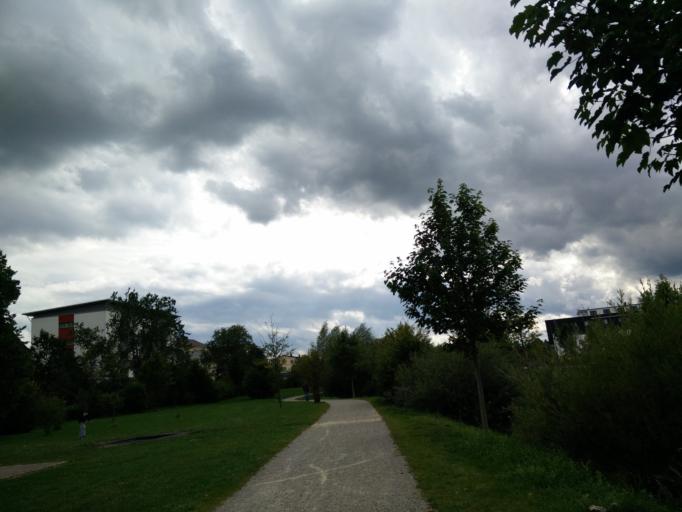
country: DE
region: Baden-Wuerttemberg
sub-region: Freiburg Region
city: Dauchingen
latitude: 48.0593
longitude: 8.5363
